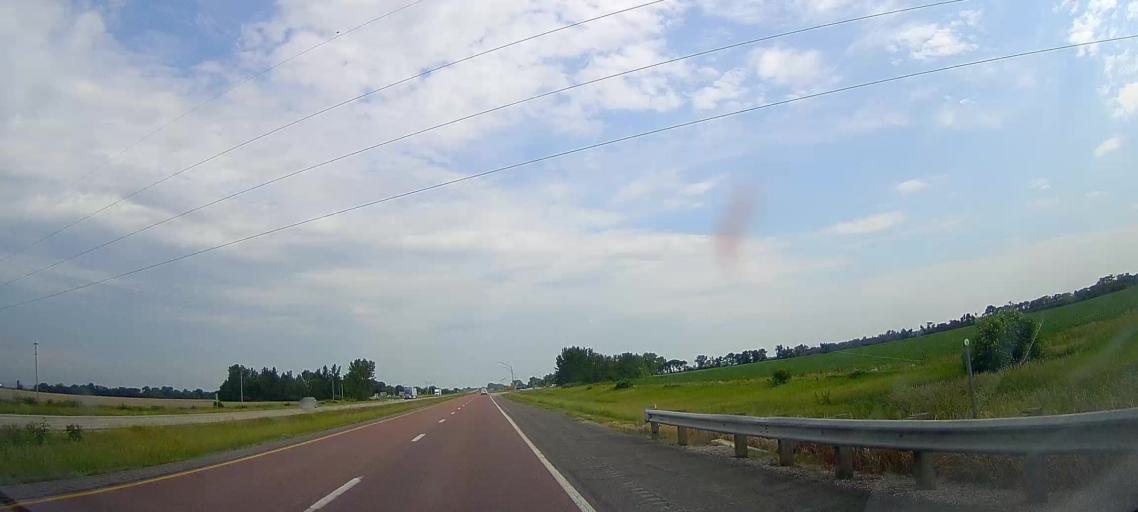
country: US
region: Iowa
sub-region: Monona County
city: Onawa
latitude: 41.9978
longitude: -96.1130
